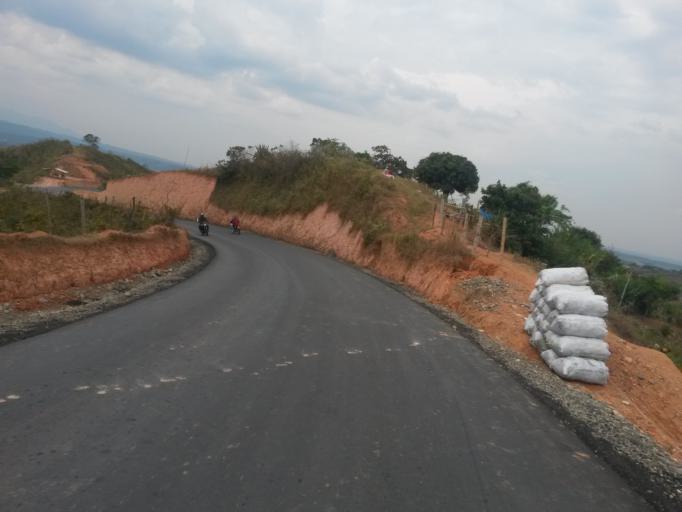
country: CO
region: Cauca
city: Buenos Aires
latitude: 3.0536
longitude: -76.6310
